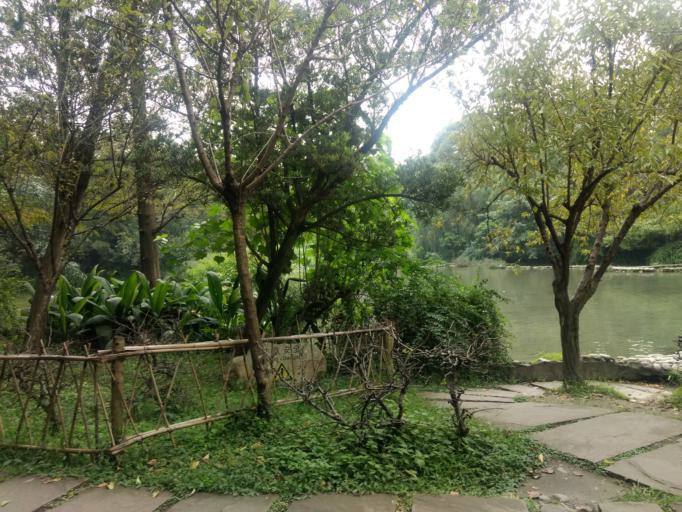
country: CN
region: Sichuan
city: Chengdu
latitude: 30.6641
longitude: 104.0262
